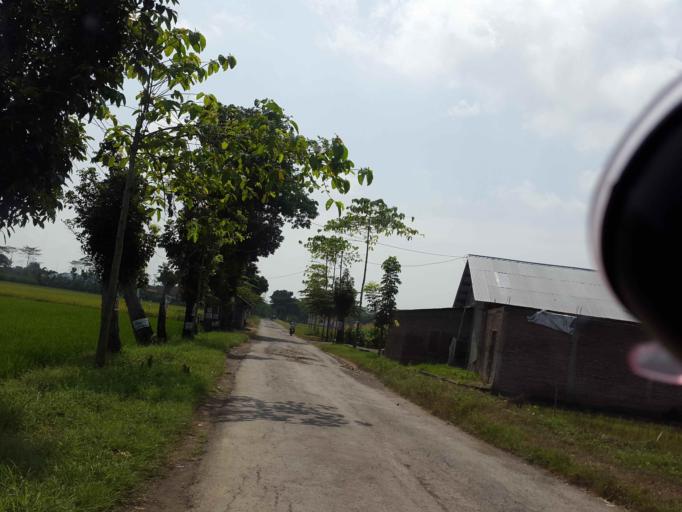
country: ID
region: Central Java
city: Pemalang
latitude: -6.9479
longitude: 109.3399
